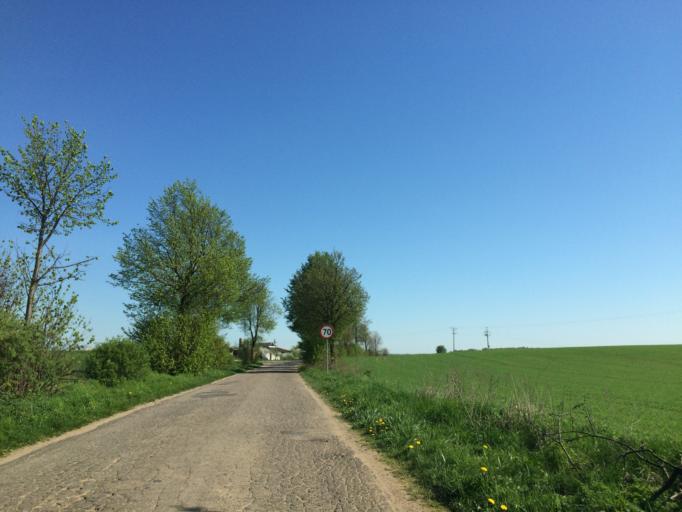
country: PL
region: Warmian-Masurian Voivodeship
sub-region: Powiat dzialdowski
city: Rybno
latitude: 53.4487
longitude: 19.9262
